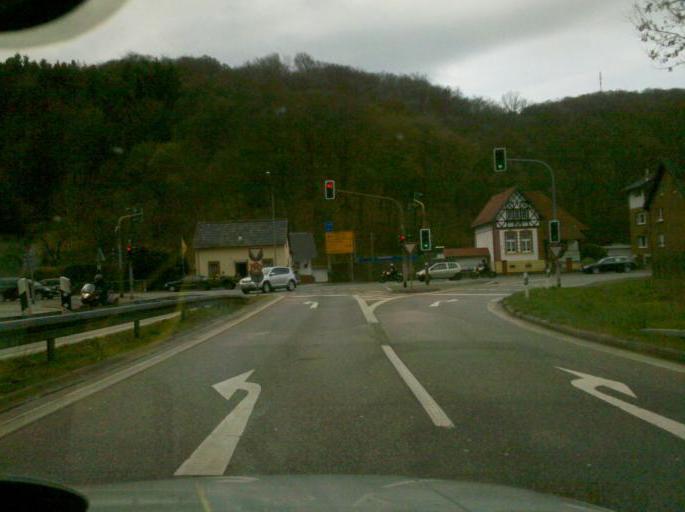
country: DE
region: North Rhine-Westphalia
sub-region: Regierungsbezirk Koln
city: Rosrath
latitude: 50.9502
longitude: 7.2185
